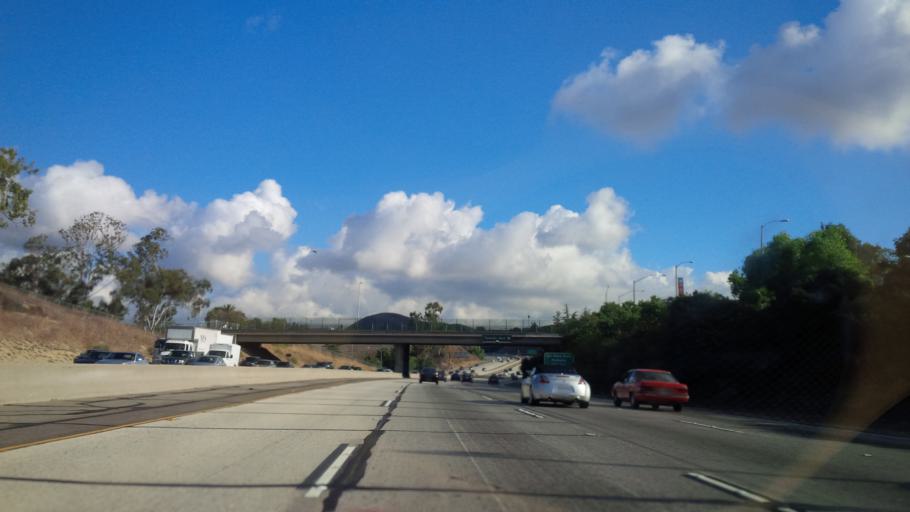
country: US
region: California
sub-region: Los Angeles County
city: Diamond Bar
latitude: 34.0354
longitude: -117.8071
